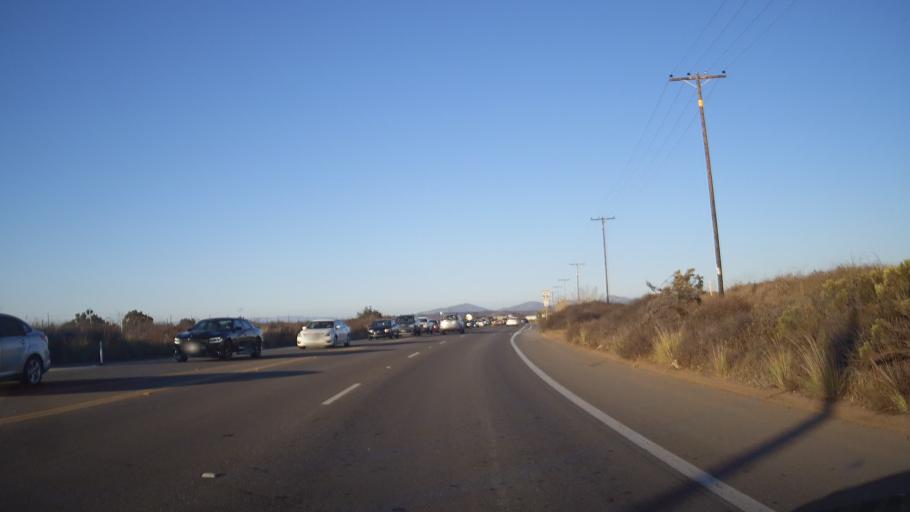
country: US
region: California
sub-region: San Diego County
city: La Mesa
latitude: 32.8443
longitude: -117.1275
